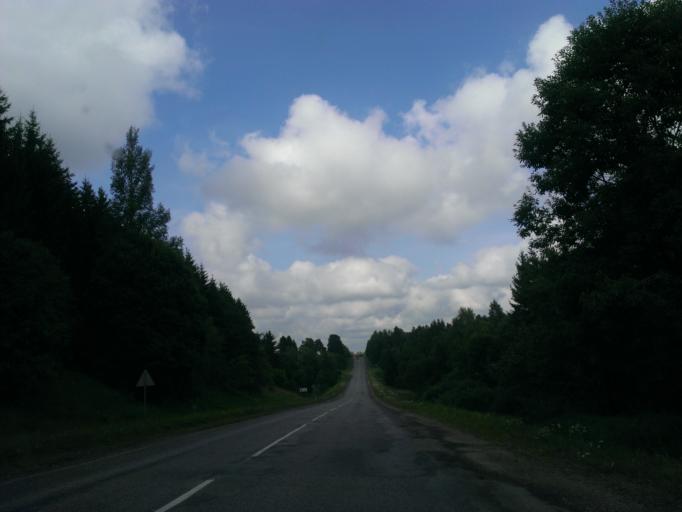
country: LV
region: Priekuli
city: Priekuli
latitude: 57.2694
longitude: 25.4677
